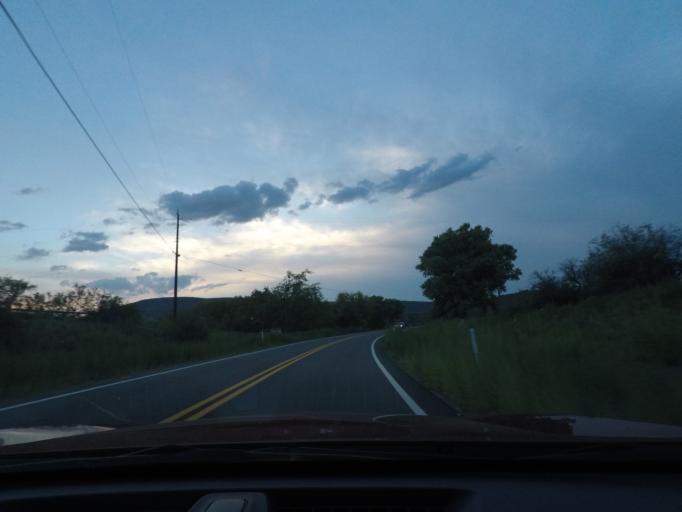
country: US
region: Arizona
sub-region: Yavapai County
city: Prescott
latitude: 34.5045
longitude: -112.6876
